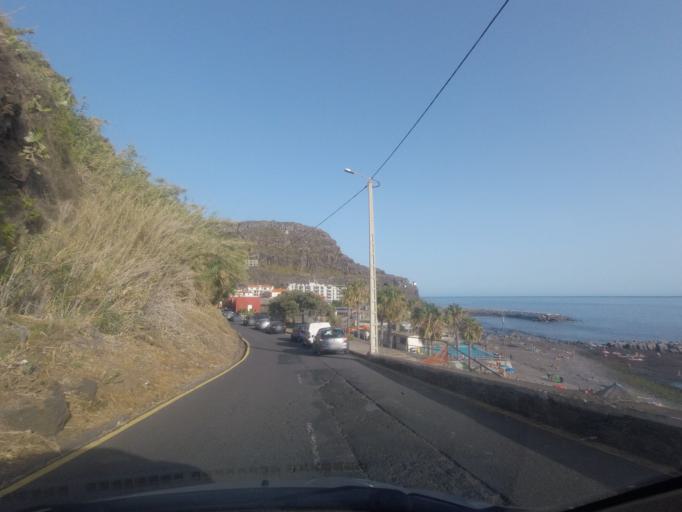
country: PT
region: Madeira
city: Ribeira Brava
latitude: 32.6718
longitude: -17.0671
